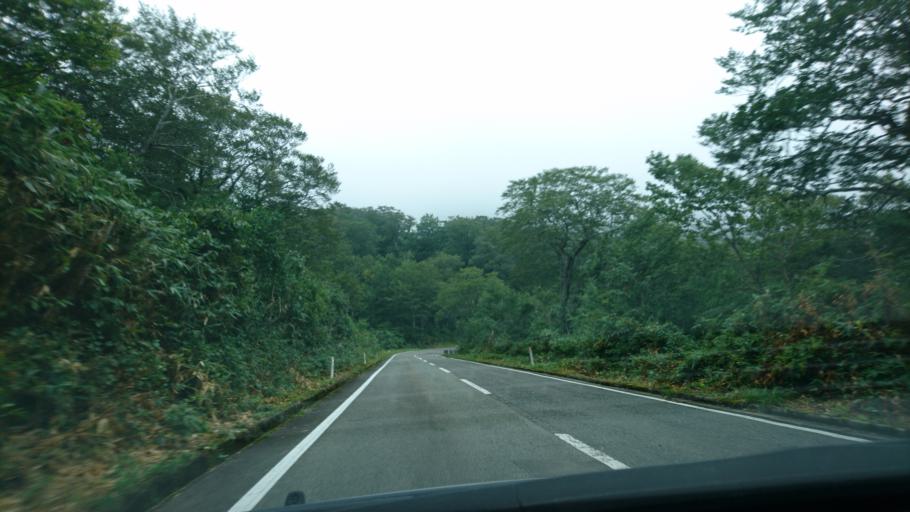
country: JP
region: Akita
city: Yuzawa
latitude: 38.9765
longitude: 140.7548
